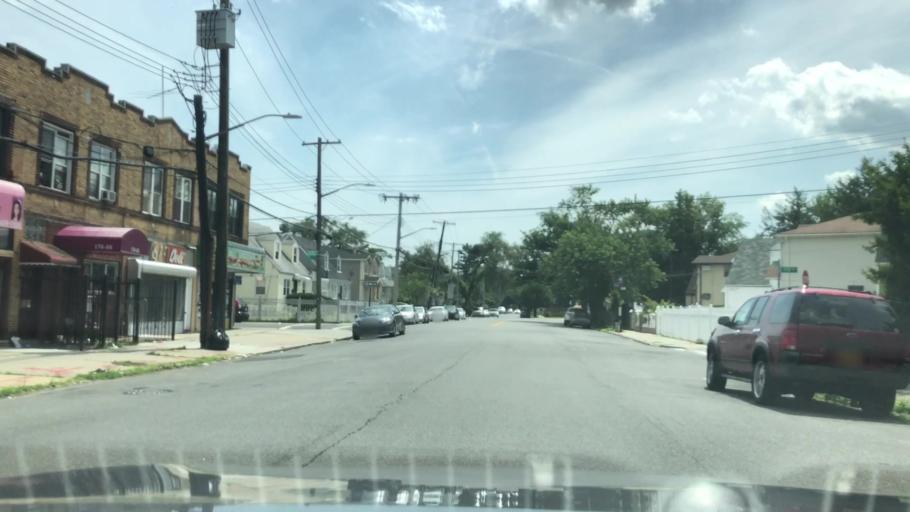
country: US
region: New York
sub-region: Queens County
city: Jamaica
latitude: 40.6976
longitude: -73.7755
